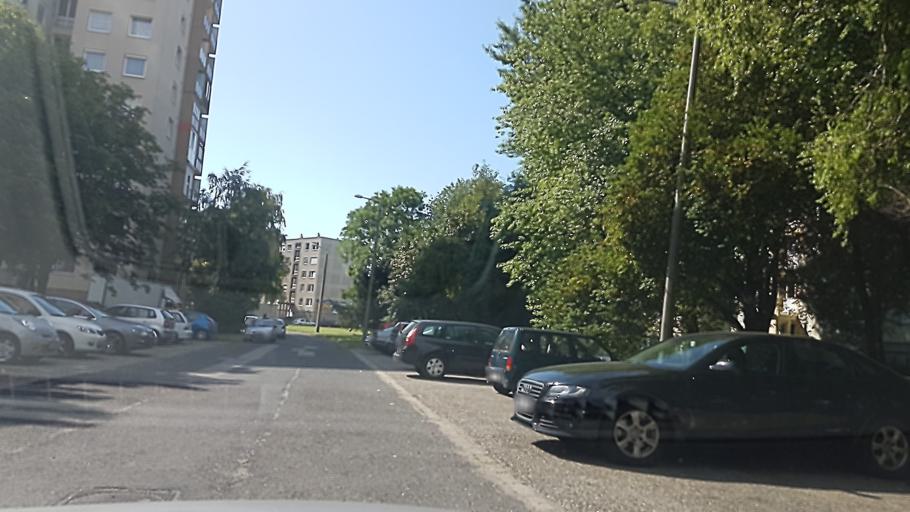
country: HU
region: Gyor-Moson-Sopron
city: Sopron
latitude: 47.6923
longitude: 16.5739
